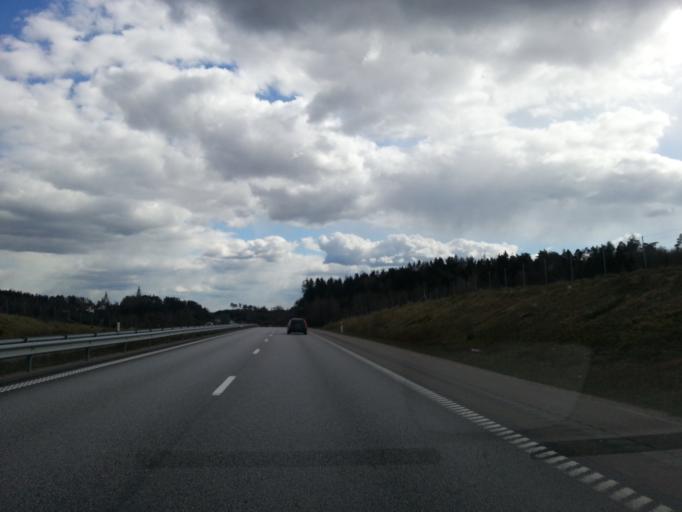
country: SE
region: Vaestra Goetaland
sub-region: Uddevalla Kommun
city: Uddevalla
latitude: 58.3423
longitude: 11.8240
